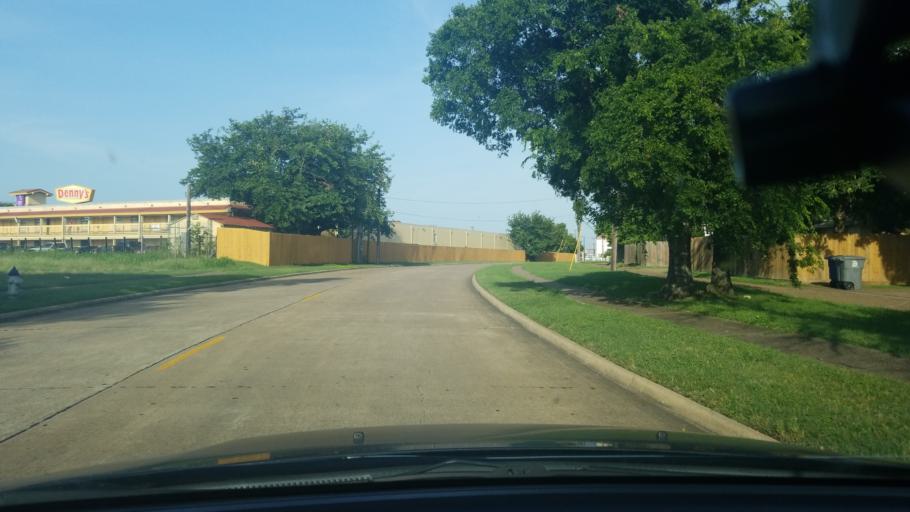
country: US
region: Texas
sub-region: Dallas County
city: Balch Springs
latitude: 32.7959
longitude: -96.6976
